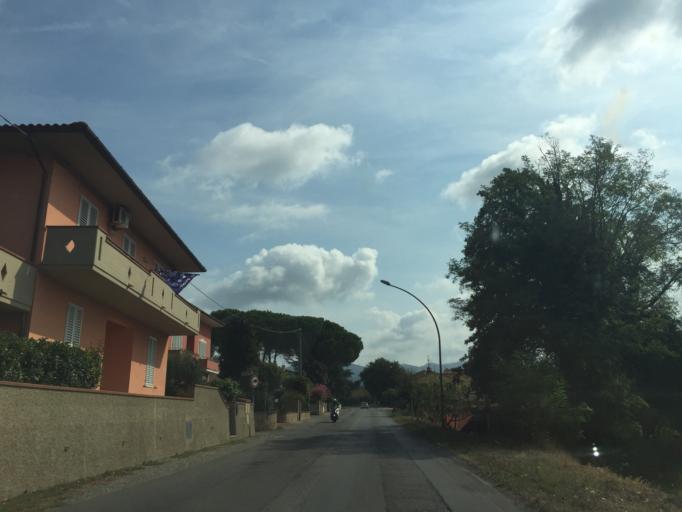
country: IT
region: Tuscany
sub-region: Provincia di Pistoia
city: San Rocco
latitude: 43.8156
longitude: 10.8665
